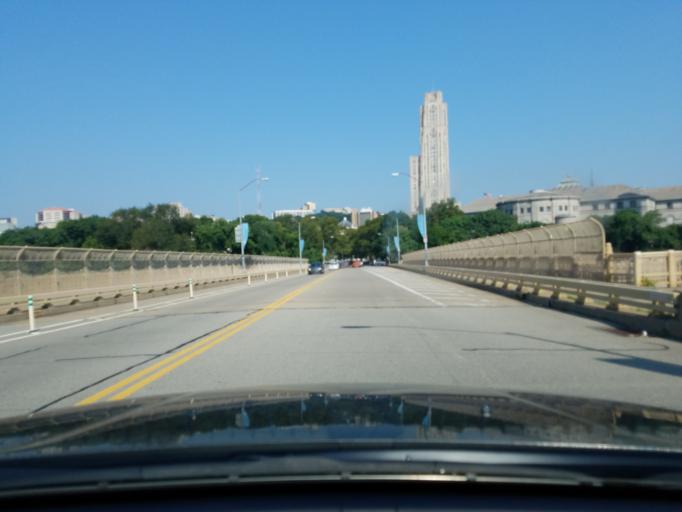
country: US
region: Pennsylvania
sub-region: Allegheny County
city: Bloomfield
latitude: 40.4410
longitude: -79.9484
